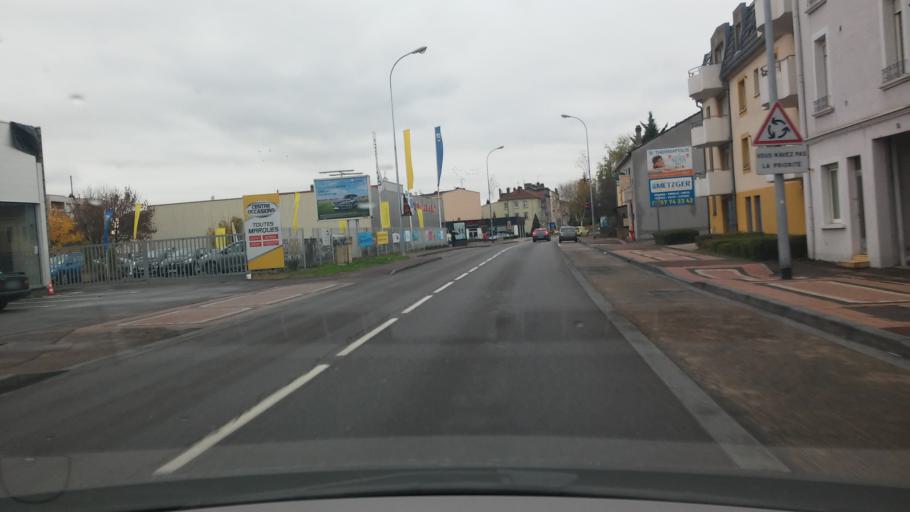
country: FR
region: Lorraine
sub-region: Departement de la Moselle
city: Talange
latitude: 49.2431
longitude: 6.1695
